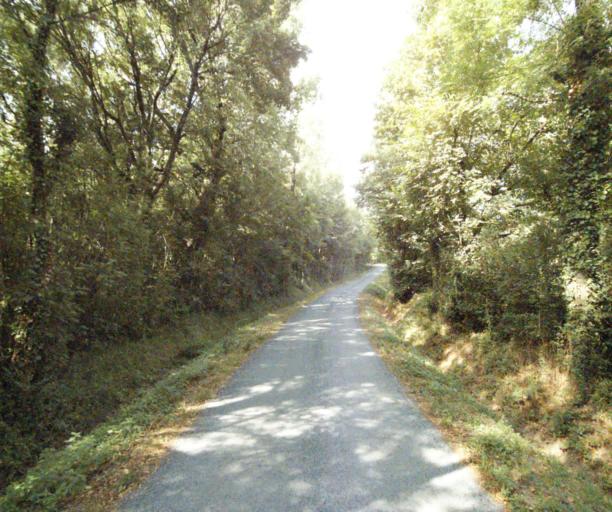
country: FR
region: Midi-Pyrenees
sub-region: Departement du Tarn
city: Soreze
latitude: 43.4699
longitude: 2.0826
